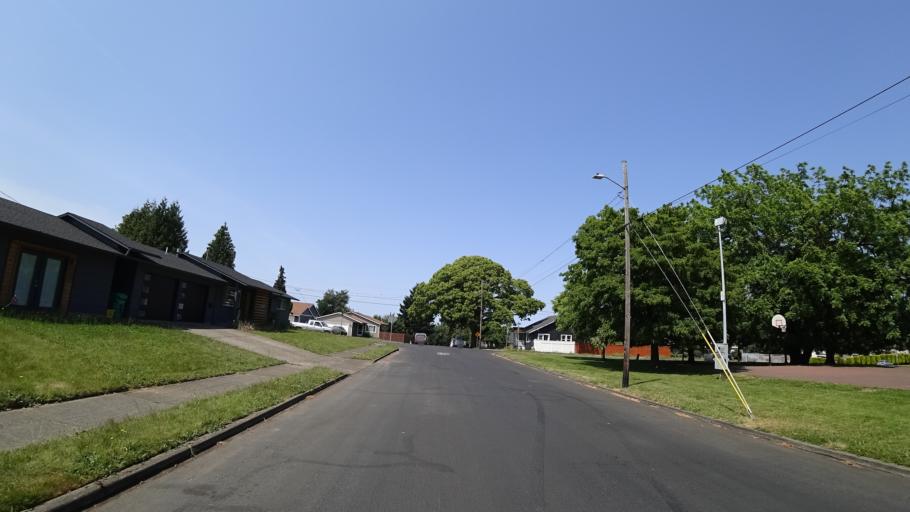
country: US
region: Washington
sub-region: Clark County
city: Vancouver
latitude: 45.5882
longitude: -122.7024
